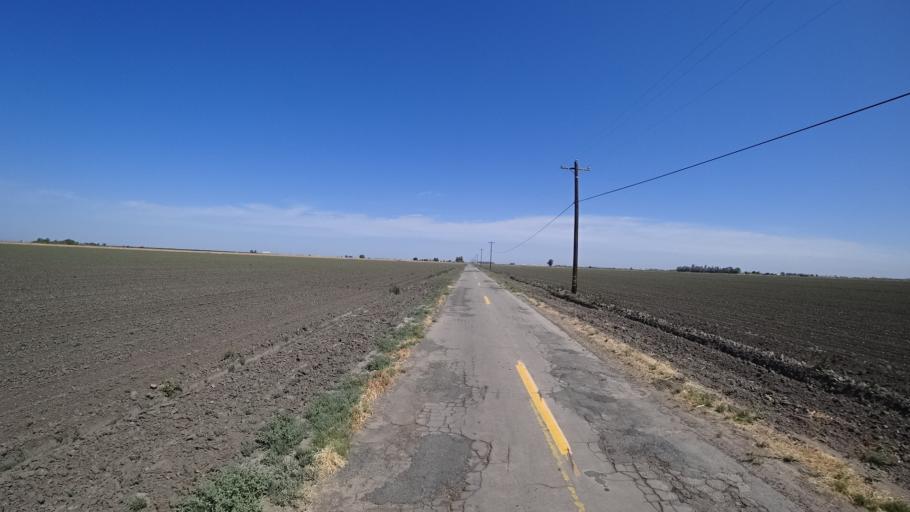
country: US
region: California
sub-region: Kings County
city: Stratford
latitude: 36.1994
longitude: -119.8161
